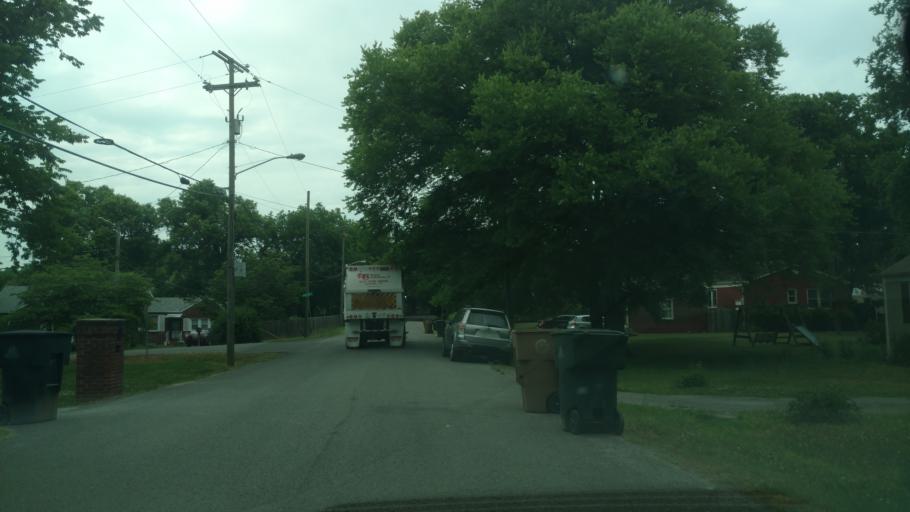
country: US
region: Tennessee
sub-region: Davidson County
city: Lakewood
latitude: 36.2093
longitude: -86.7087
